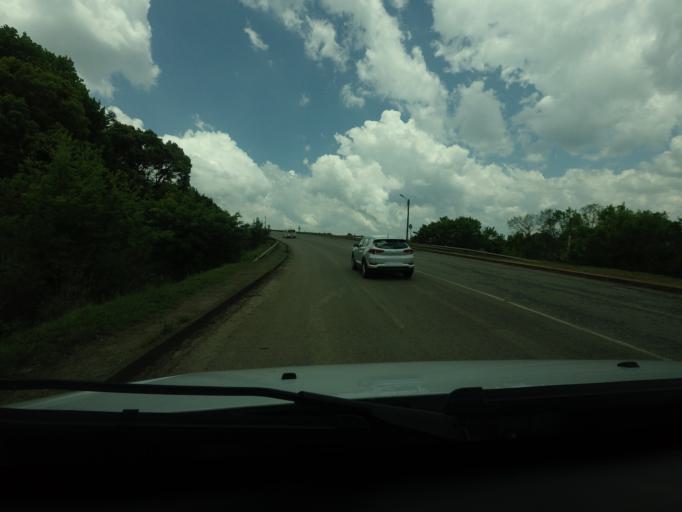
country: ZA
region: Mpumalanga
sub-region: Ehlanzeni District
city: Graksop
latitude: -24.9321
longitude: 30.8377
